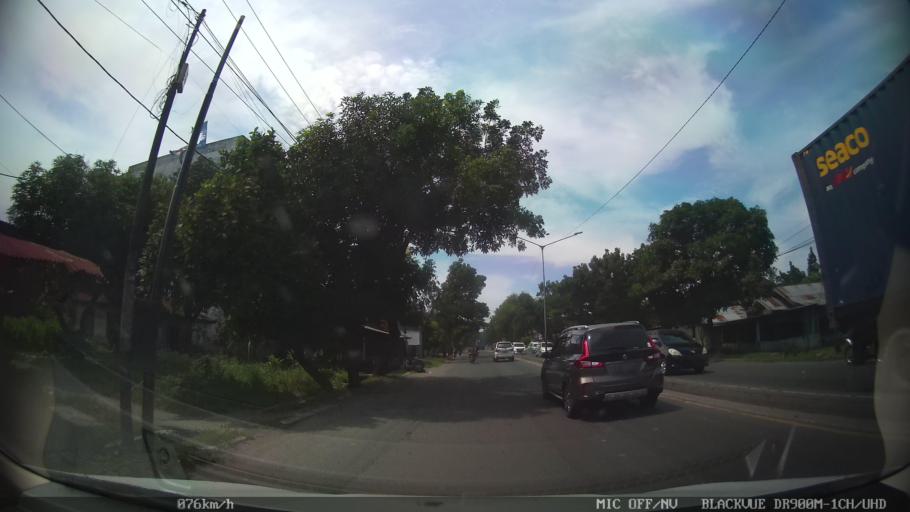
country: ID
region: North Sumatra
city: Labuhan Deli
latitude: 3.6683
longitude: 98.6672
